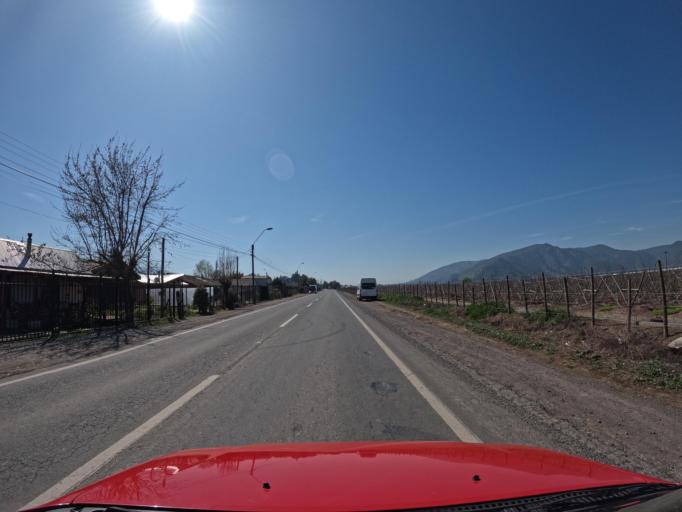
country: CL
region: Maule
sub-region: Provincia de Curico
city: Rauco
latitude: -35.0364
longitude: -71.4483
